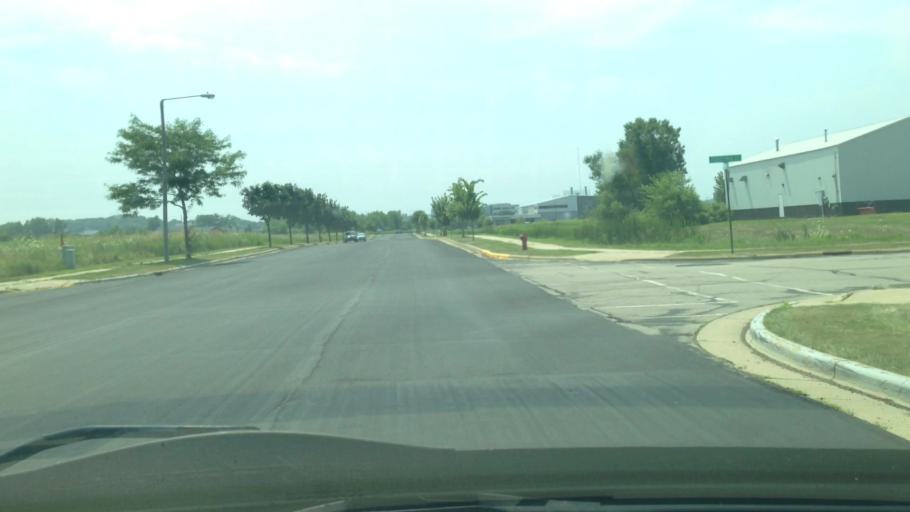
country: US
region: Wisconsin
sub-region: Dane County
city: Middleton
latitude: 43.1102
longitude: -89.5212
